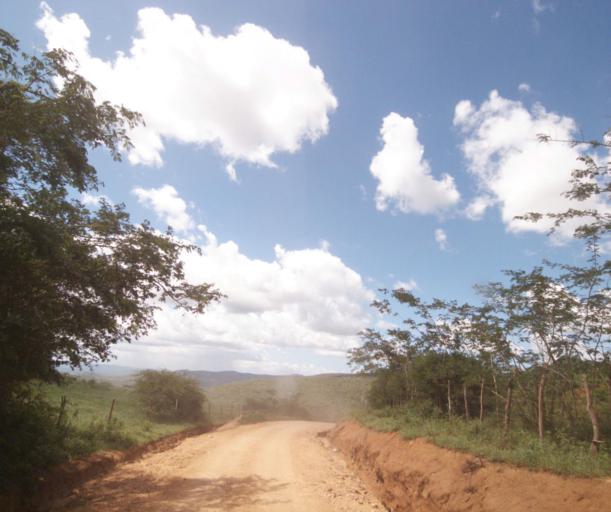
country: BR
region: Bahia
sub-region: Pocoes
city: Pocoes
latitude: -14.2974
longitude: -40.6797
